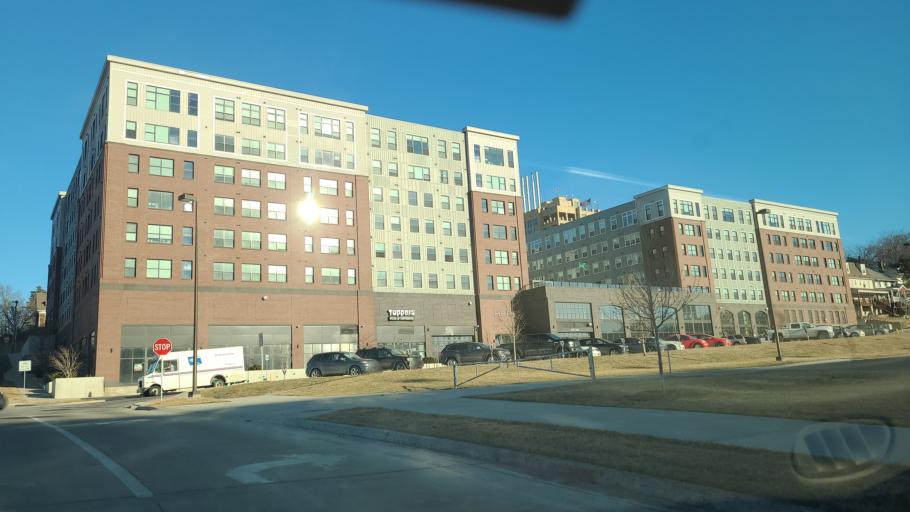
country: US
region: Kansas
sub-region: Douglas County
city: Lawrence
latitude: 38.9638
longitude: -95.2446
